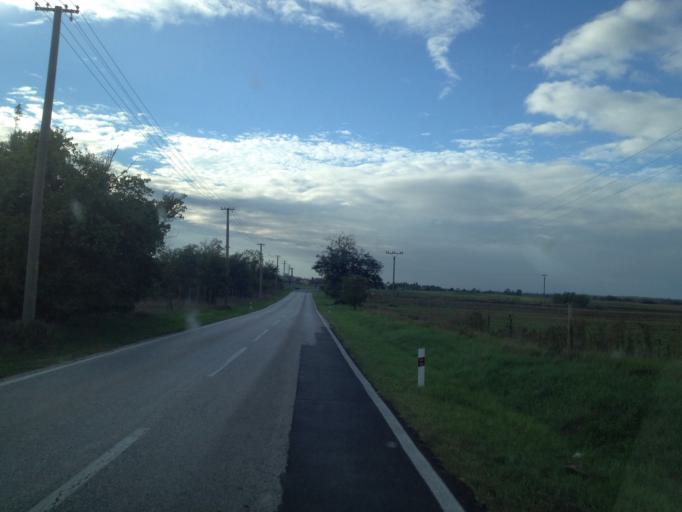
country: HU
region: Komarom-Esztergom
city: Dunaalmas
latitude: 47.7463
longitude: 18.3352
